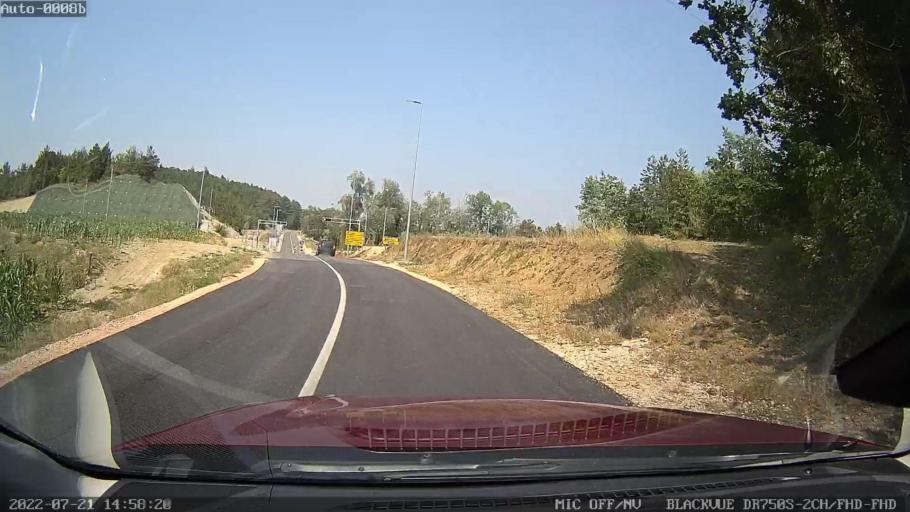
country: HR
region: Istarska
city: Pazin
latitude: 45.2151
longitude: 13.9567
